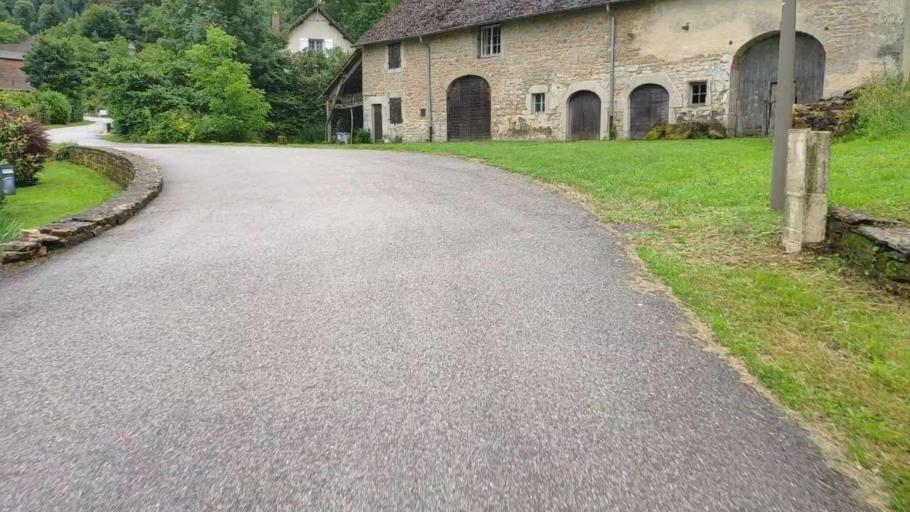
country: FR
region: Franche-Comte
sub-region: Departement du Jura
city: Poligny
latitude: 46.7827
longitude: 5.6140
